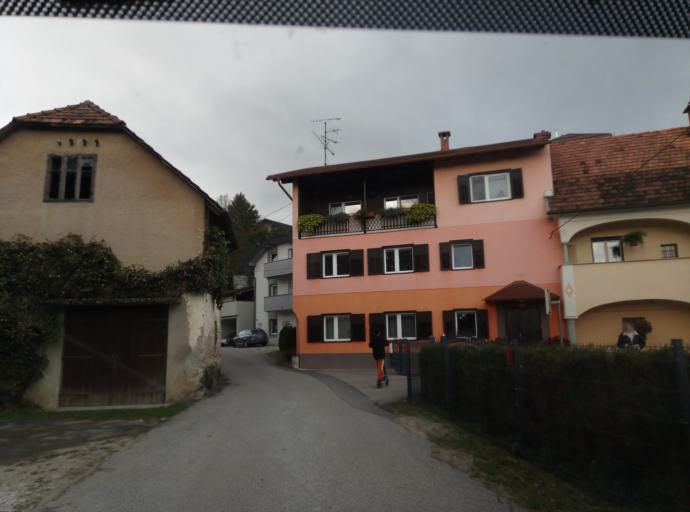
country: SI
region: Medvode
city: Zgornje Pirnice
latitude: 46.1286
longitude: 14.4892
